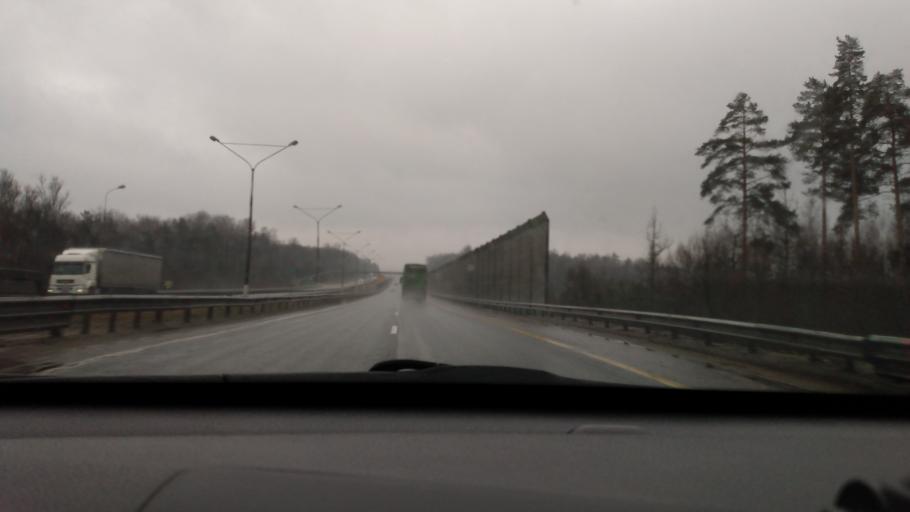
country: RU
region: Moskovskaya
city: Stupino
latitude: 54.8710
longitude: 38.0283
